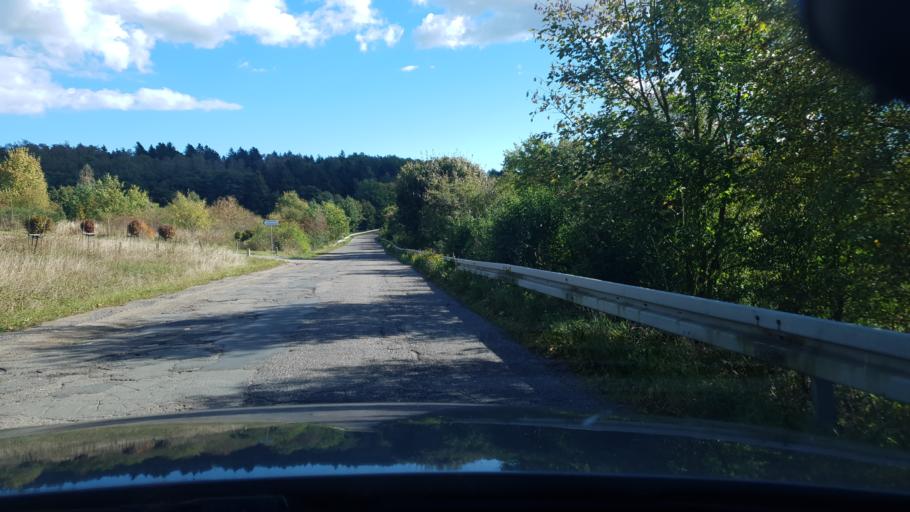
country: PL
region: Pomeranian Voivodeship
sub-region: Powiat pucki
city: Zelistrzewo
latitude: 54.6899
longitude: 18.4221
